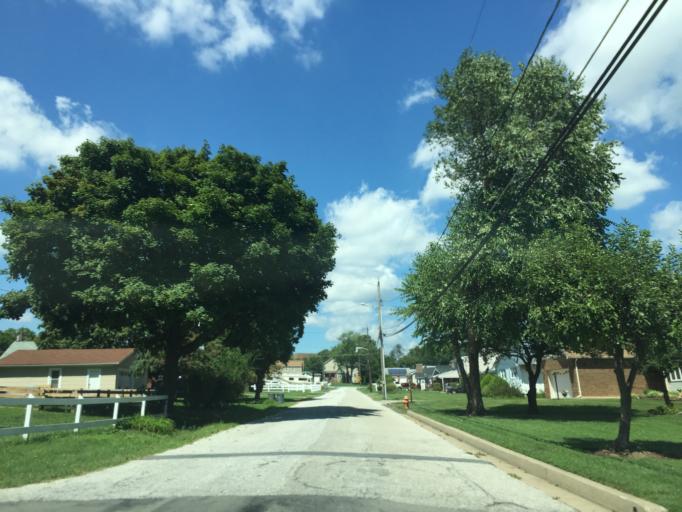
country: US
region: Maryland
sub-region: Baltimore County
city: Dundalk
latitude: 39.2644
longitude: -76.5080
